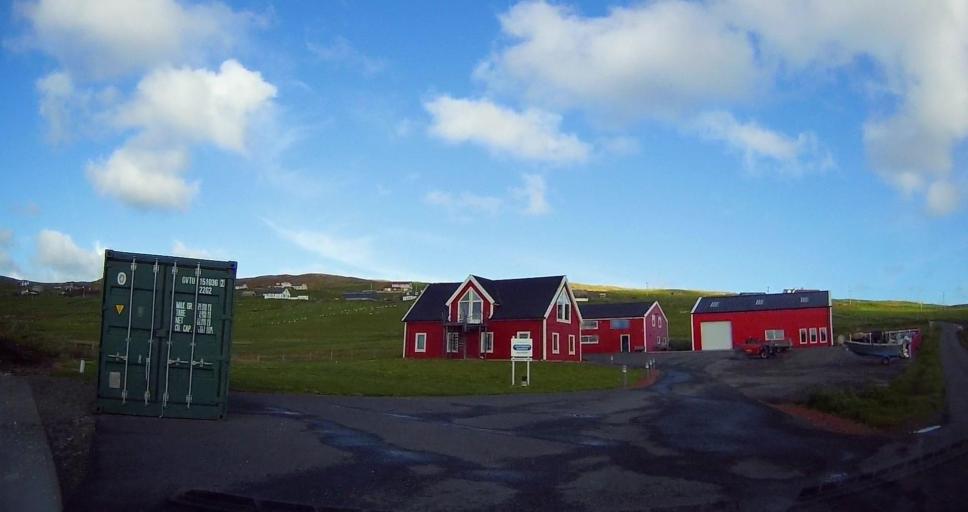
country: GB
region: Scotland
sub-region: Shetland Islands
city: Shetland
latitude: 60.3693
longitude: -1.1292
